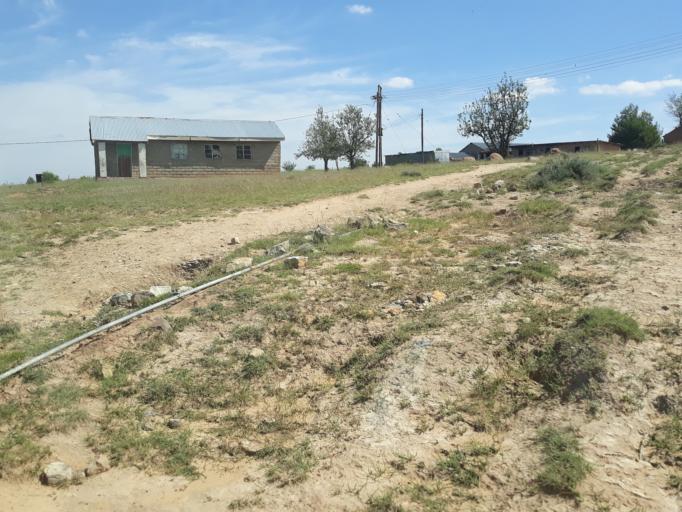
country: LS
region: Mohale's Hoek District
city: Mohale's Hoek
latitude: -30.1009
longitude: 27.4777
